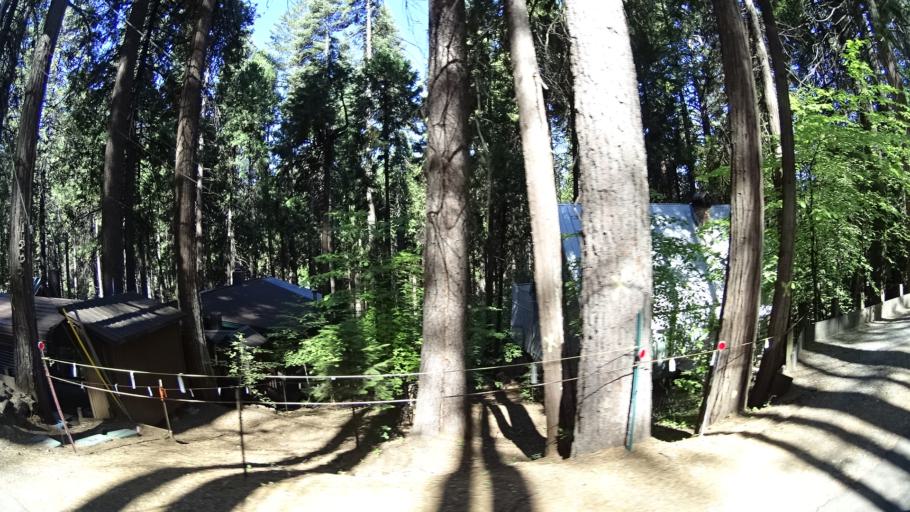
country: US
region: California
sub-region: Calaveras County
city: Arnold
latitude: 38.2445
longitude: -120.3318
